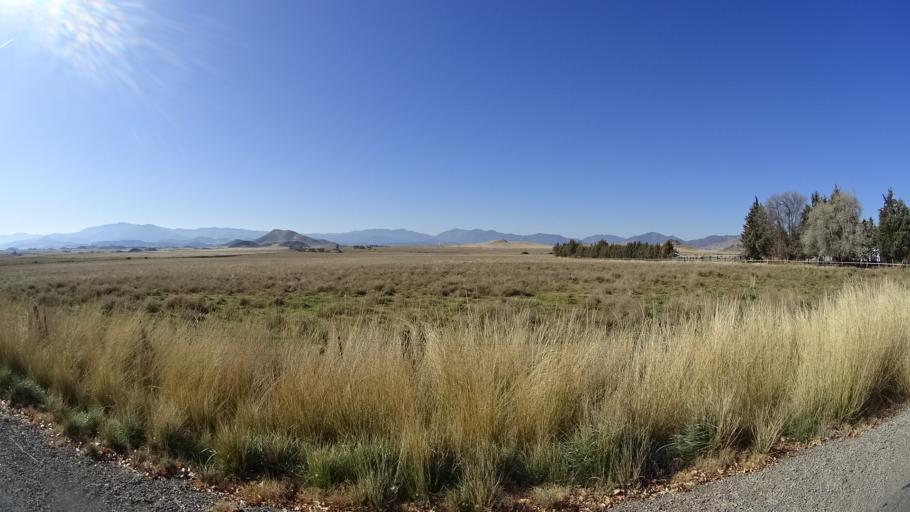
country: US
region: California
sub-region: Siskiyou County
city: Montague
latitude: 41.7326
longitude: -122.4574
